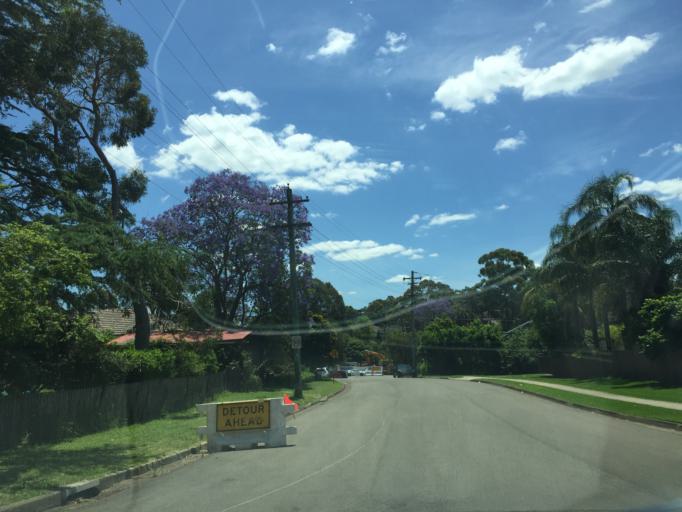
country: AU
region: New South Wales
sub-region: Parramatta
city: Dundas Valley
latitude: -33.7875
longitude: 151.0702
